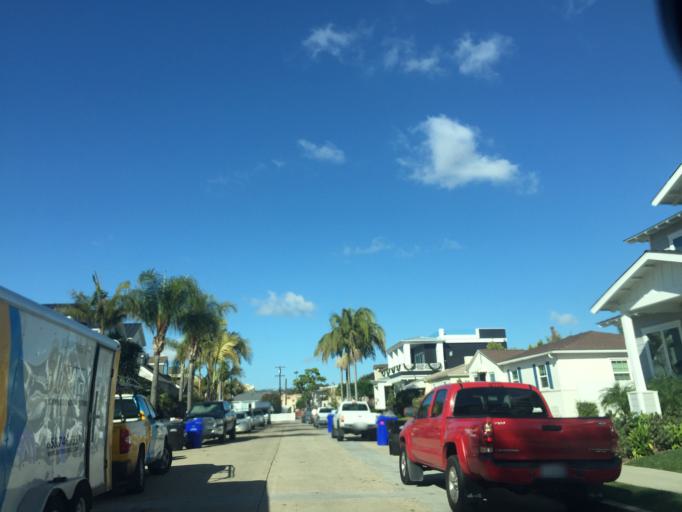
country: US
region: California
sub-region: San Diego County
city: La Jolla
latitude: 32.7856
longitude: -117.2381
